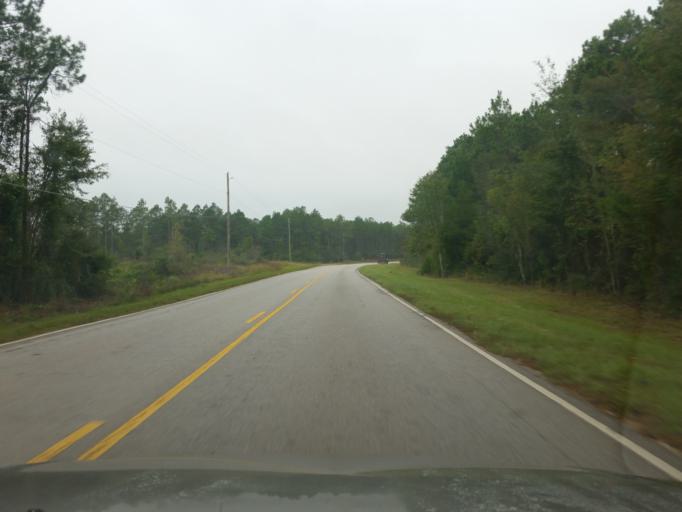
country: US
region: Florida
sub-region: Escambia County
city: Cantonment
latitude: 30.5974
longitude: -87.3837
